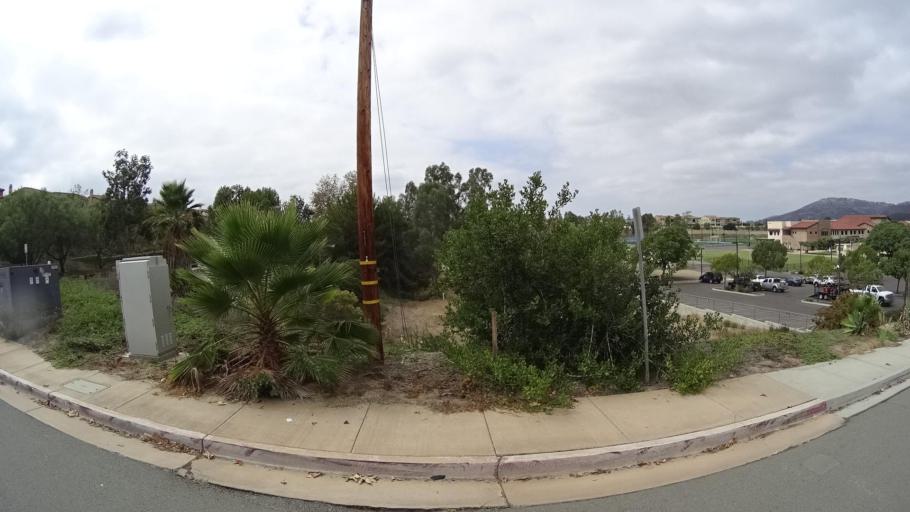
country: US
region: California
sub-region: San Diego County
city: Fairbanks Ranch
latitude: 33.0220
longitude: -117.1355
